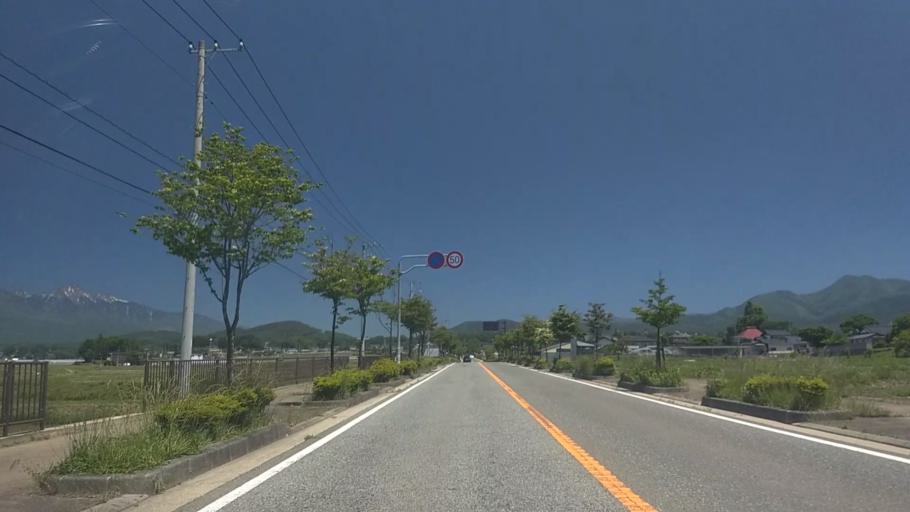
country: JP
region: Yamanashi
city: Nirasaki
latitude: 35.8255
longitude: 138.4290
